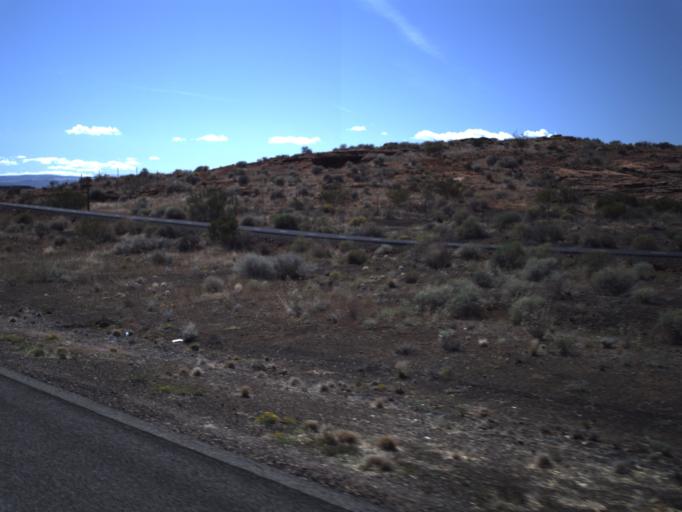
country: US
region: Utah
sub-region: Washington County
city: Saint George
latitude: 37.1409
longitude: -113.6046
